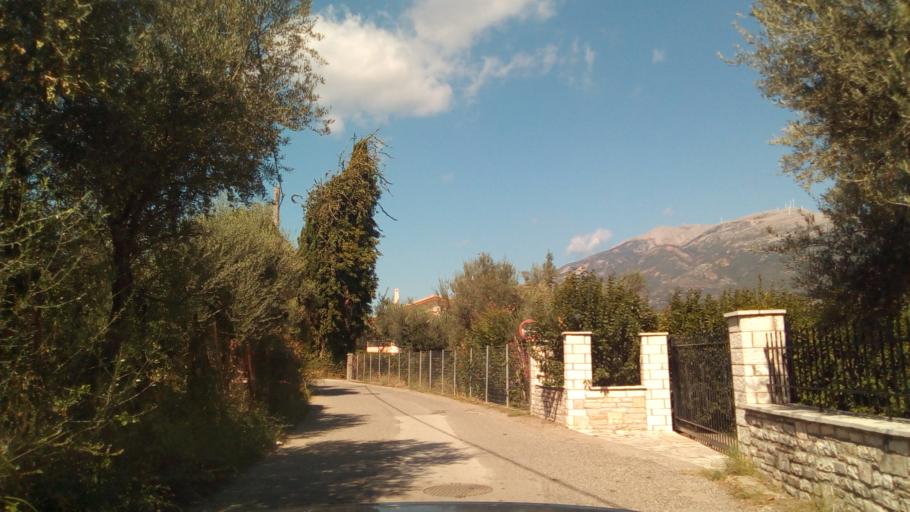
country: GR
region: West Greece
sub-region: Nomos Aitolias kai Akarnanias
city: Nafpaktos
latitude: 38.3838
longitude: 21.8053
